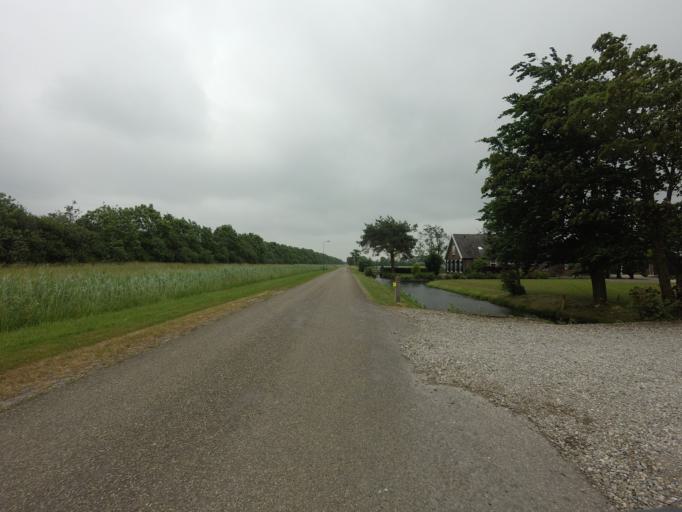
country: NL
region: Utrecht
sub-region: Gemeente IJsselstein
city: IJsselstein
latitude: 52.0703
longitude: 5.0432
